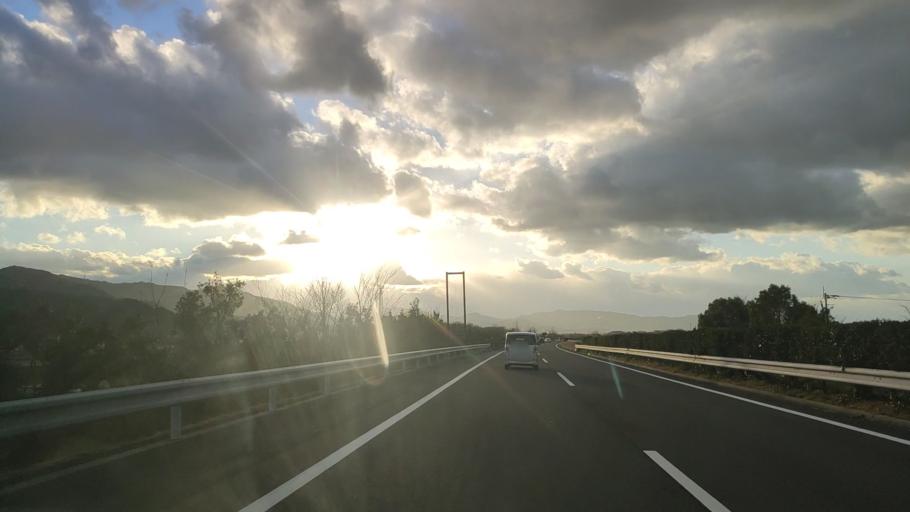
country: JP
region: Ehime
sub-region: Shikoku-chuo Shi
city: Matsuyama
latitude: 33.7866
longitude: 132.8764
